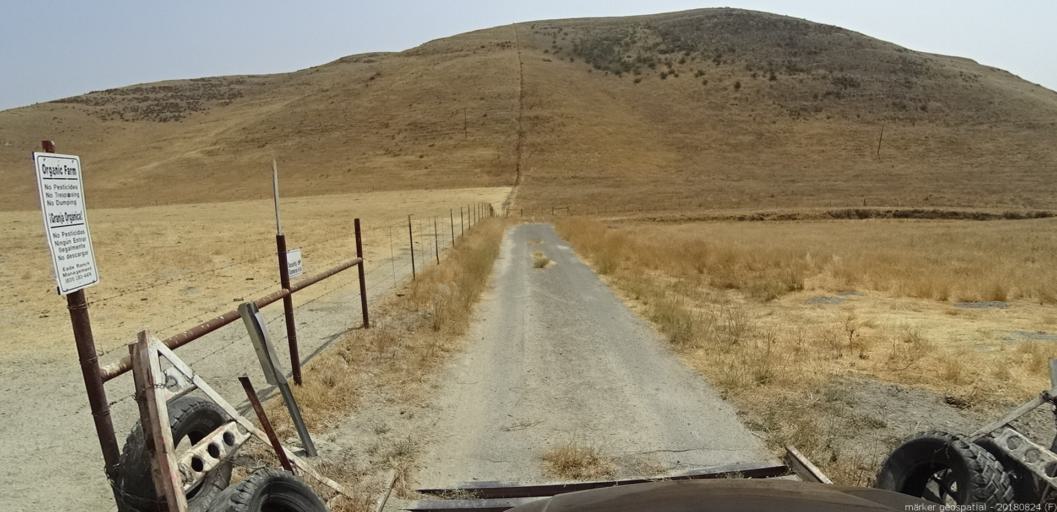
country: US
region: California
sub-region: Monterey County
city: King City
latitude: 36.1982
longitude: -120.9489
